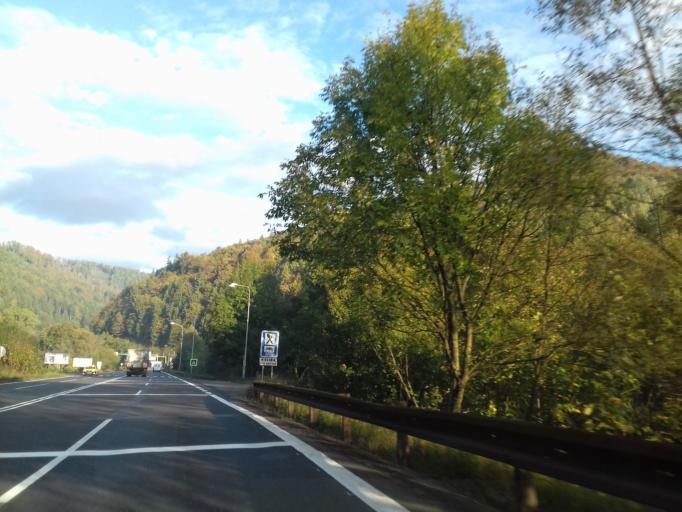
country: SK
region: Banskobystricky
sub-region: Okres Banska Bystrica
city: Banska Bystrica
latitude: 48.7873
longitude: 19.1086
